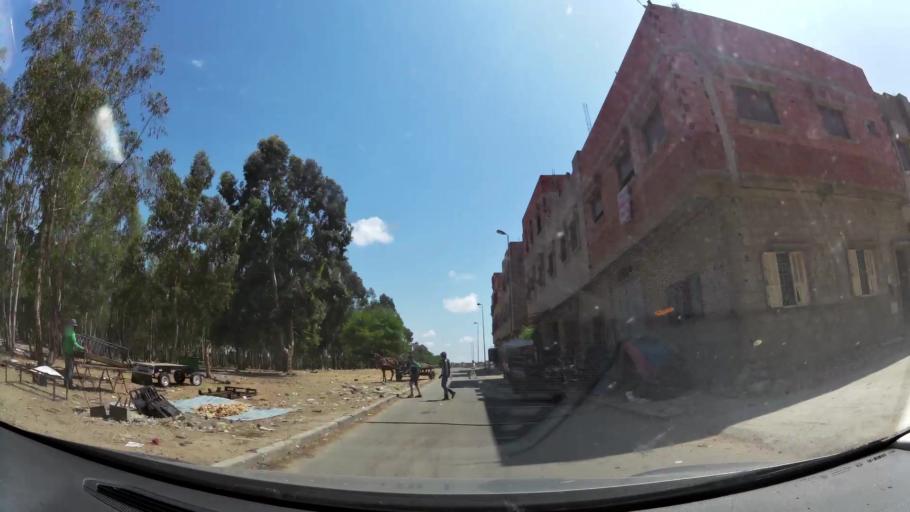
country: MA
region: Gharb-Chrarda-Beni Hssen
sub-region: Kenitra Province
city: Kenitra
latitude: 34.2405
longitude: -6.5370
